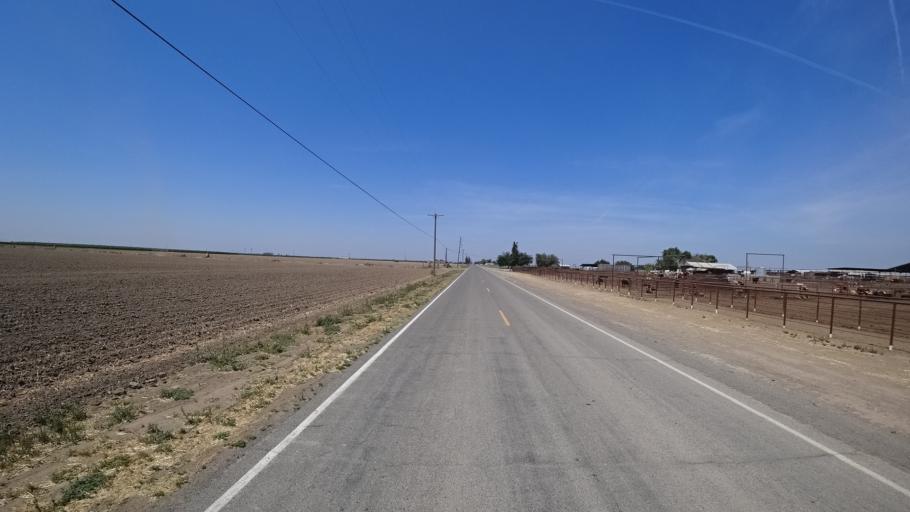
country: US
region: California
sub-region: Kings County
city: Lucerne
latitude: 36.4014
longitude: -119.5584
